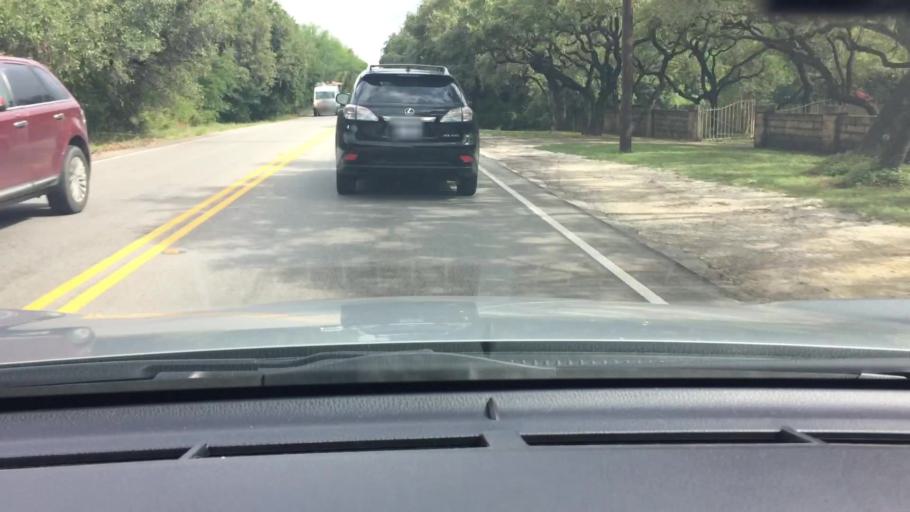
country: US
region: Texas
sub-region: Bexar County
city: Castle Hills
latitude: 29.5470
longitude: -98.5357
